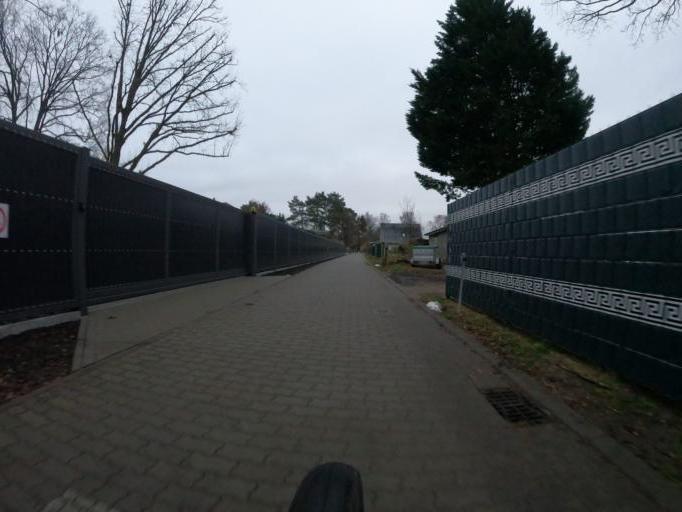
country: DE
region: Brandenburg
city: Schulzendorf
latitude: 52.3602
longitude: 13.5978
